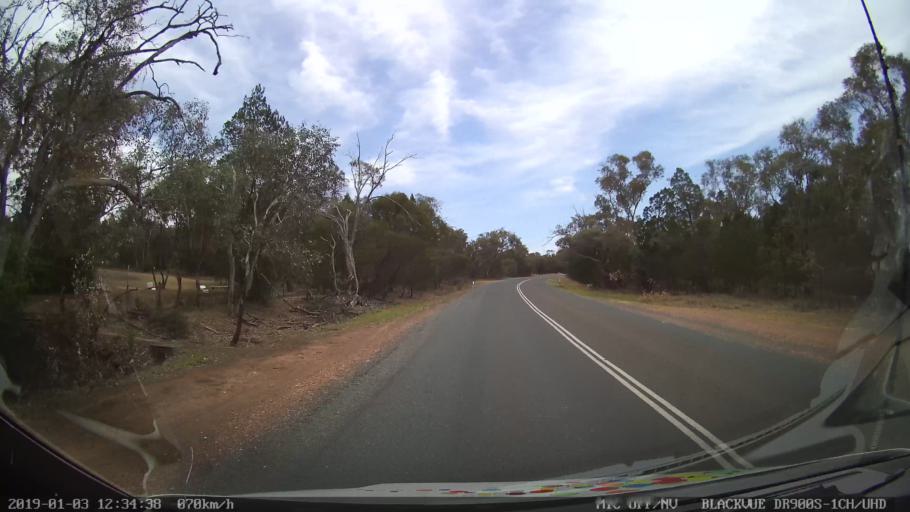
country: AU
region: New South Wales
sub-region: Weddin
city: Grenfell
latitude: -33.8745
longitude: 148.1661
